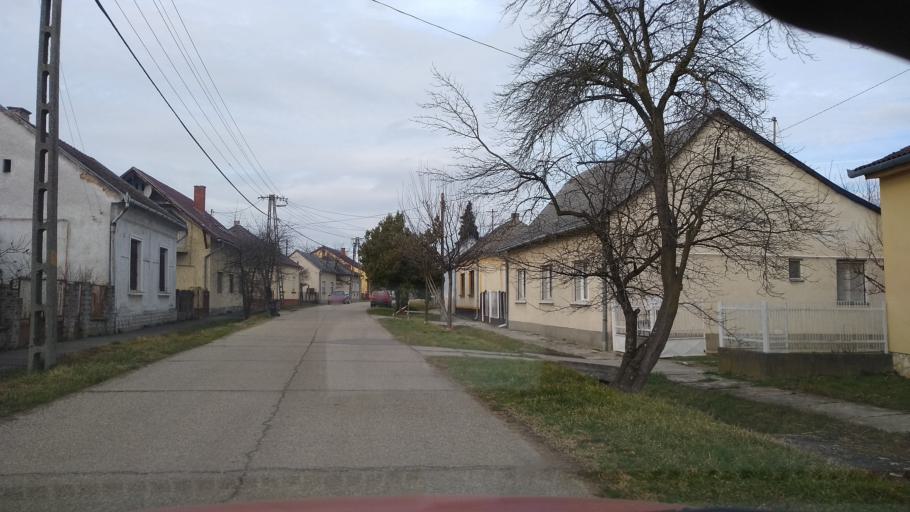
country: HU
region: Somogy
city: Barcs
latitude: 45.9611
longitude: 17.4475
